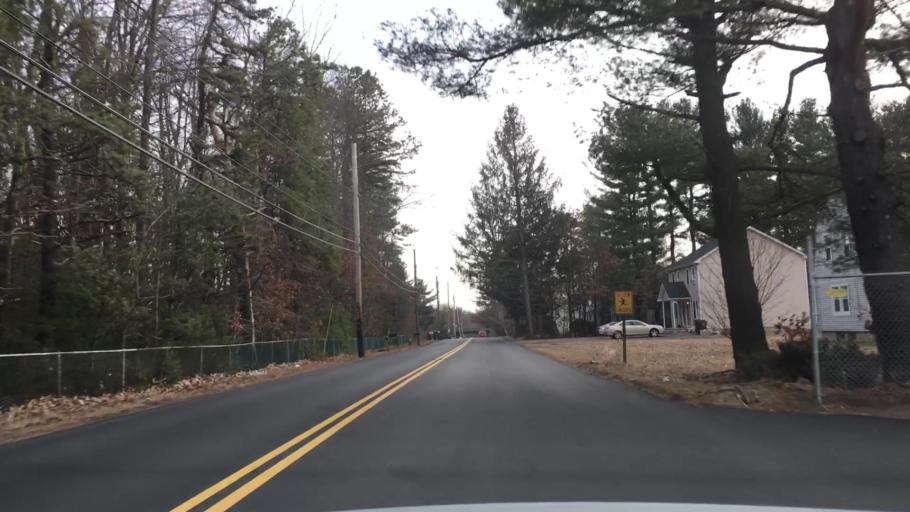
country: US
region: Massachusetts
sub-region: Hampden County
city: Westfield
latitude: 42.1489
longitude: -72.7414
